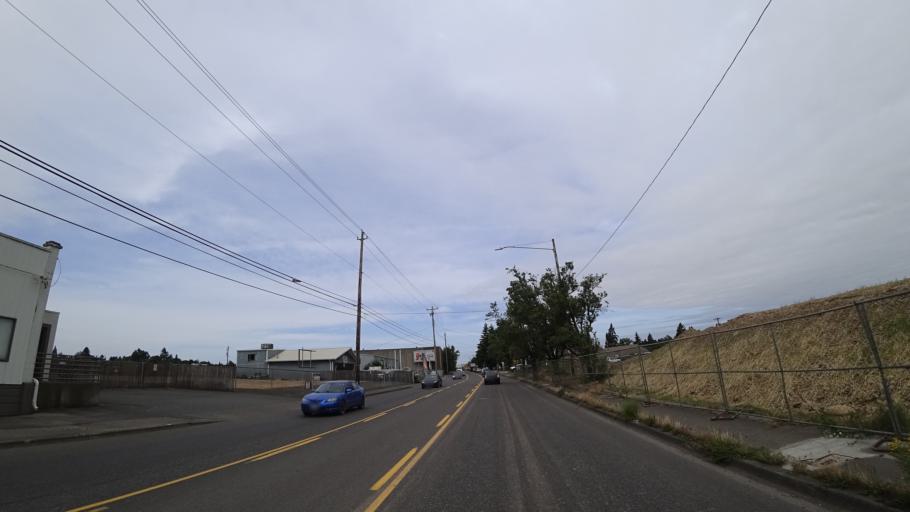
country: US
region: Oregon
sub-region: Multnomah County
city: Lents
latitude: 45.5674
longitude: -122.5918
